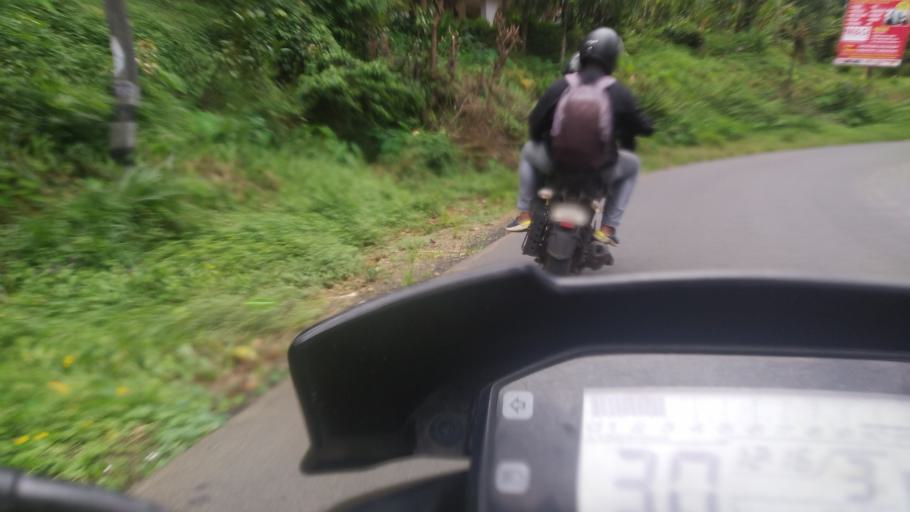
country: IN
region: Kerala
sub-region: Idukki
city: Munnar
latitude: 10.0141
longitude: 77.0101
